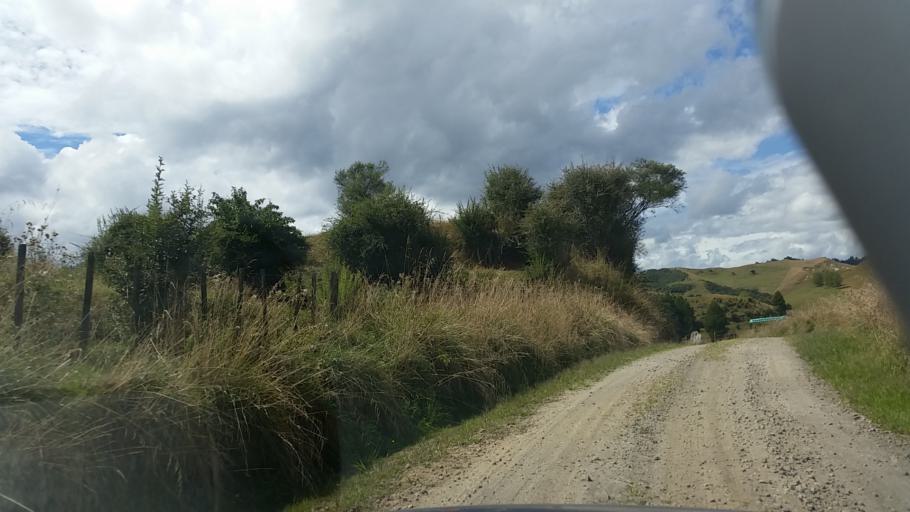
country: NZ
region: Taranaki
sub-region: South Taranaki District
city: Eltham
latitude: -39.2564
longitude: 174.5679
